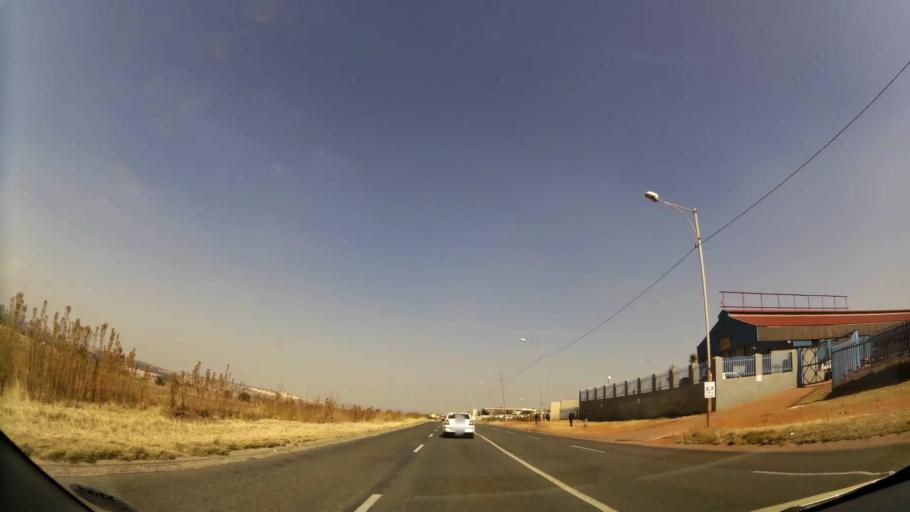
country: ZA
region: Gauteng
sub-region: City of Johannesburg Metropolitan Municipality
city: Roodepoort
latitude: -26.1620
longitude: 27.8057
